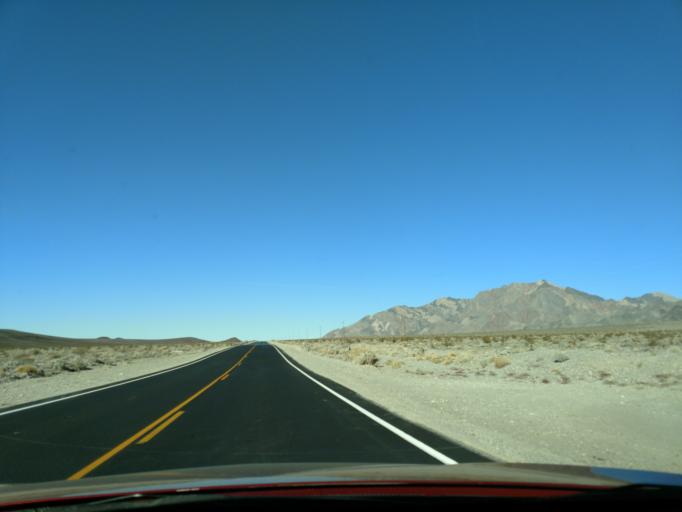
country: US
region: Nevada
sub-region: Nye County
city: Pahrump
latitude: 36.3234
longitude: -116.5595
